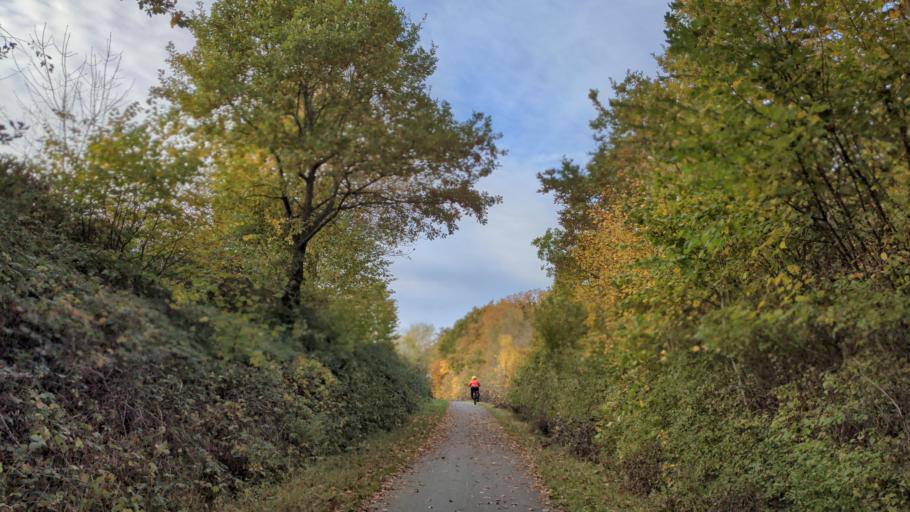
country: DE
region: Schleswig-Holstein
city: Eutin
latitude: 54.1296
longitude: 10.5684
